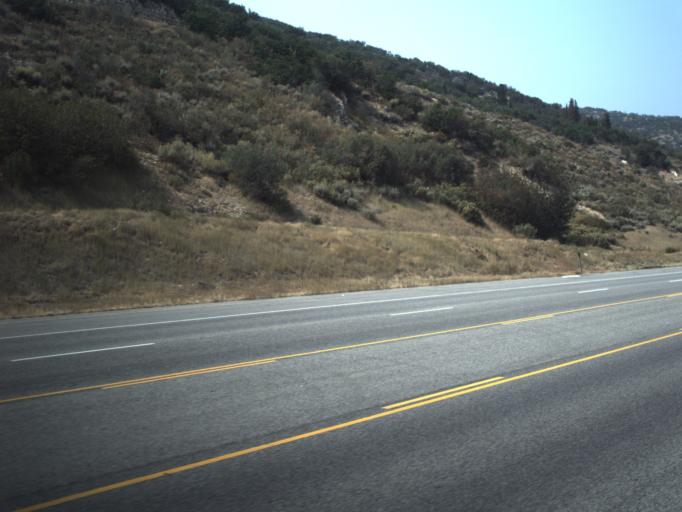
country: US
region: Utah
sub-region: Summit County
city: Snyderville
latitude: 40.7000
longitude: -111.5446
